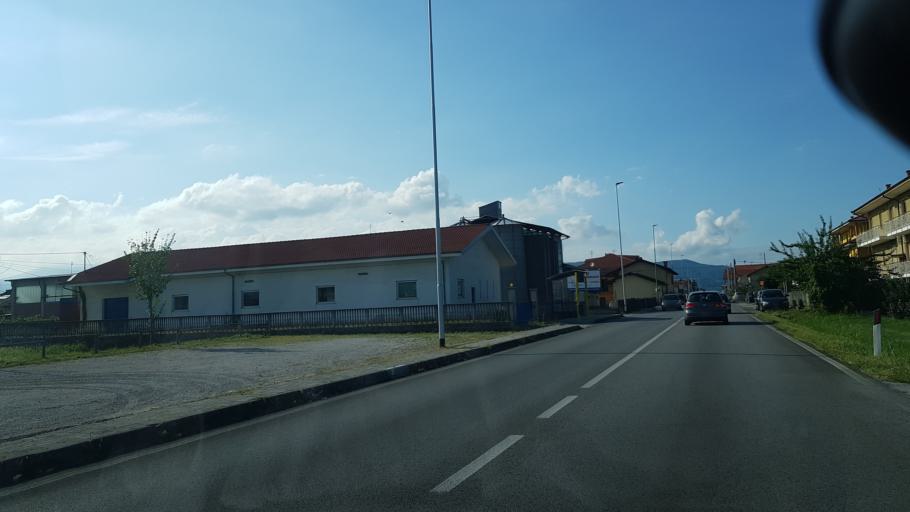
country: IT
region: Piedmont
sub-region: Provincia di Cuneo
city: Roata Rossi
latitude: 44.4760
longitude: 7.5081
